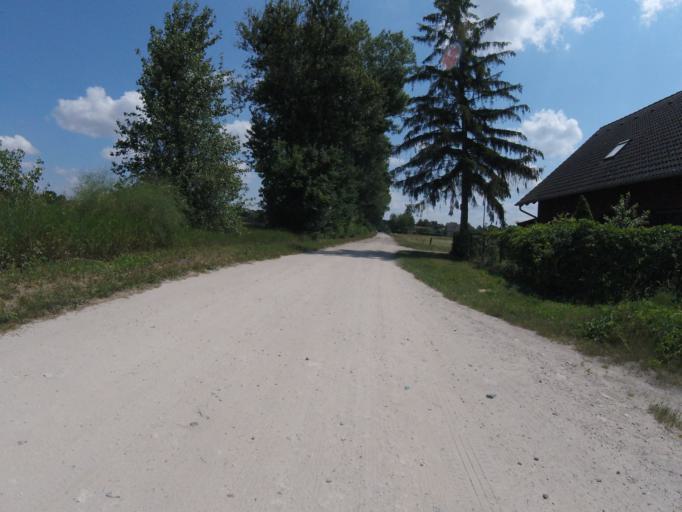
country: DE
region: Brandenburg
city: Bestensee
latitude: 52.2593
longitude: 13.7261
